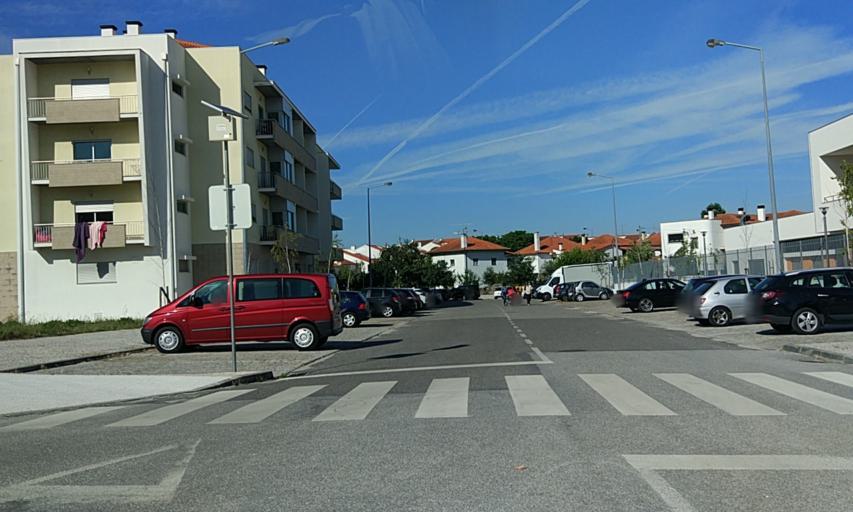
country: PT
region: Viseu
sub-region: Viseu
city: Viseu
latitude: 40.6459
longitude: -7.9092
